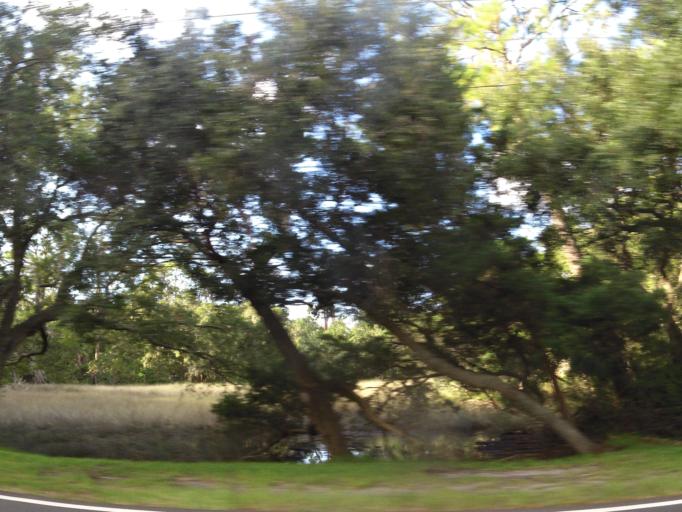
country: US
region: Georgia
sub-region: Glynn County
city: Saint Simons Island
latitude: 31.1827
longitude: -81.3720
